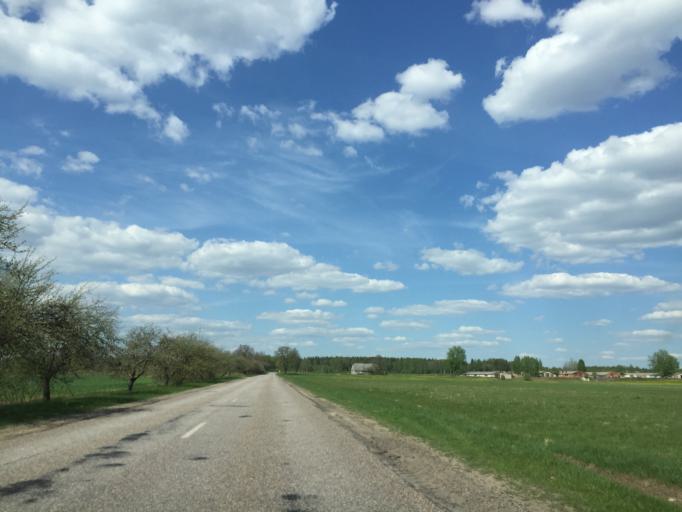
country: LV
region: Limbazu Rajons
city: Limbazi
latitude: 57.3953
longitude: 24.6903
